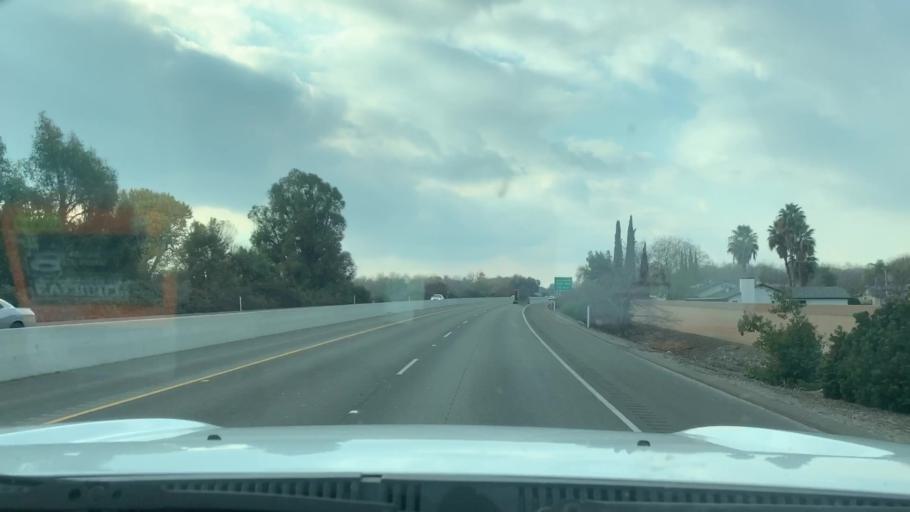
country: US
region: California
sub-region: Kings County
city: Lemoore
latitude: 36.2918
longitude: -119.7699
